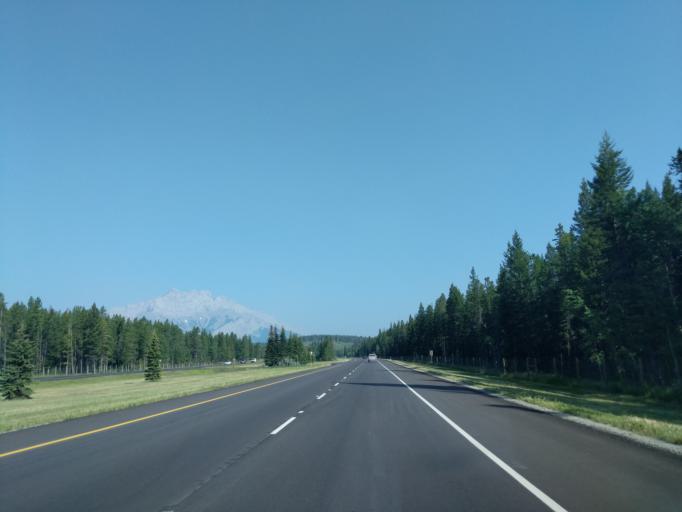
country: CA
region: Alberta
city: Canmore
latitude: 51.1535
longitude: -115.4325
